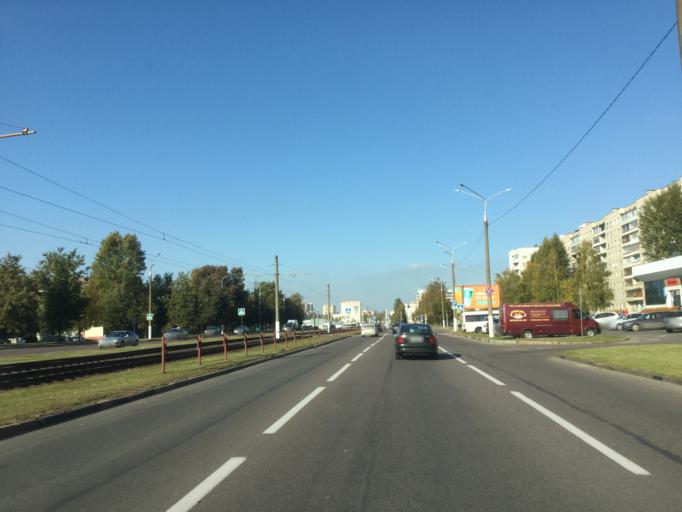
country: BY
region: Vitebsk
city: Vitebsk
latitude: 55.1818
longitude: 30.2302
